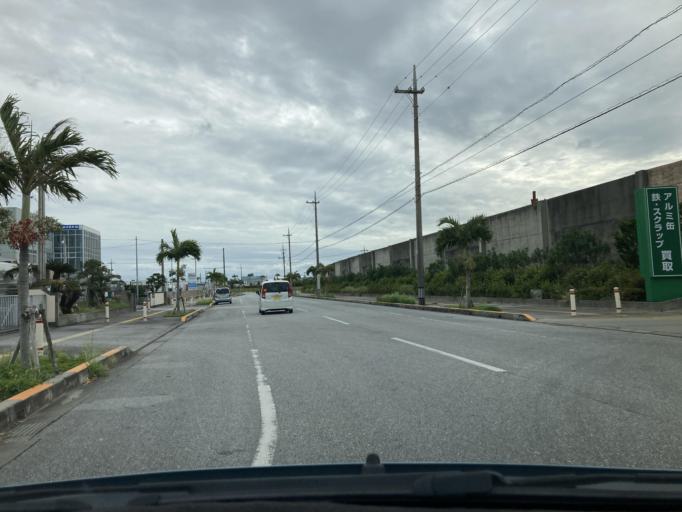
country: JP
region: Okinawa
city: Itoman
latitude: 26.1540
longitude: 127.6556
